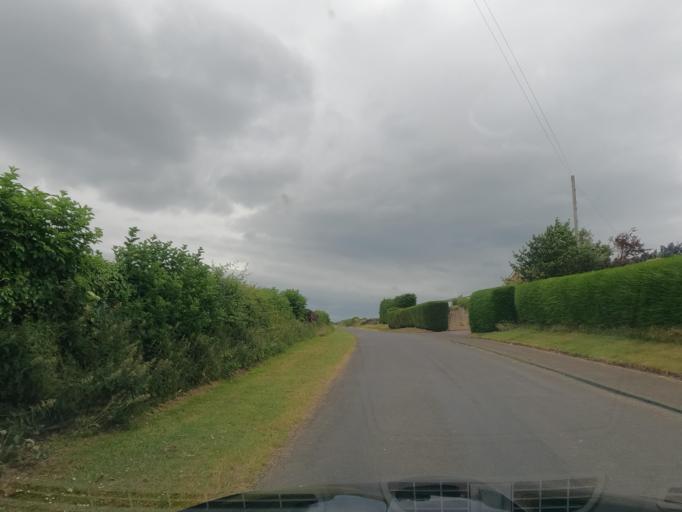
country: GB
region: England
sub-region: Northumberland
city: Ancroft
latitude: 55.6693
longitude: -2.0195
